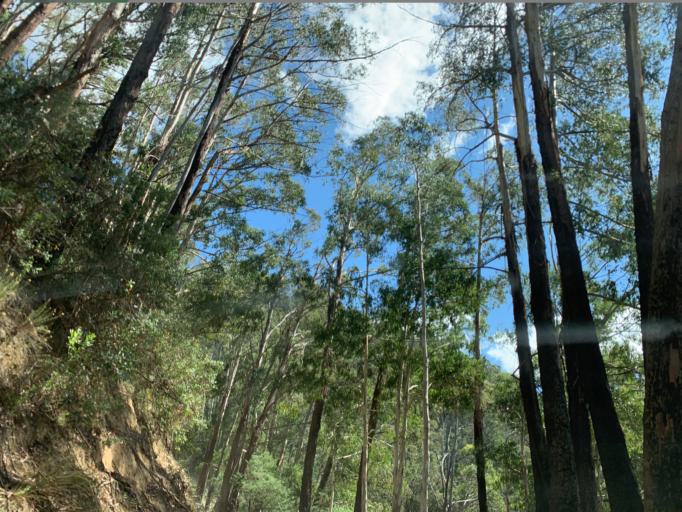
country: AU
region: Victoria
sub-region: Mansfield
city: Mansfield
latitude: -37.0981
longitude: 146.4955
